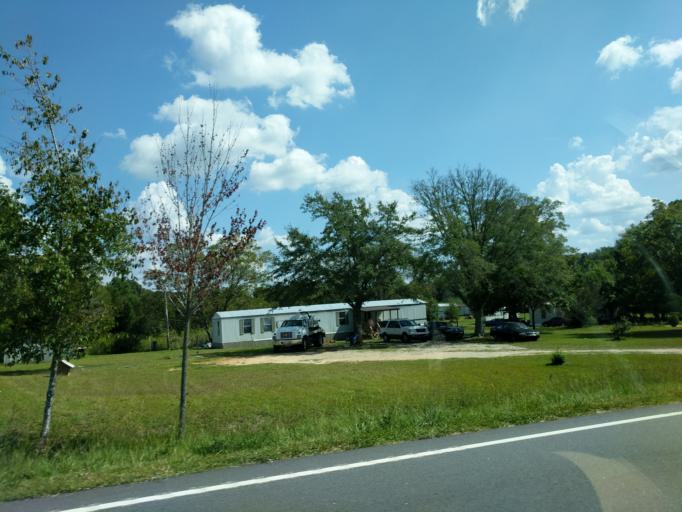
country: US
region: South Carolina
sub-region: Spartanburg County
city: Woodruff
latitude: 34.6460
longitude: -82.0924
